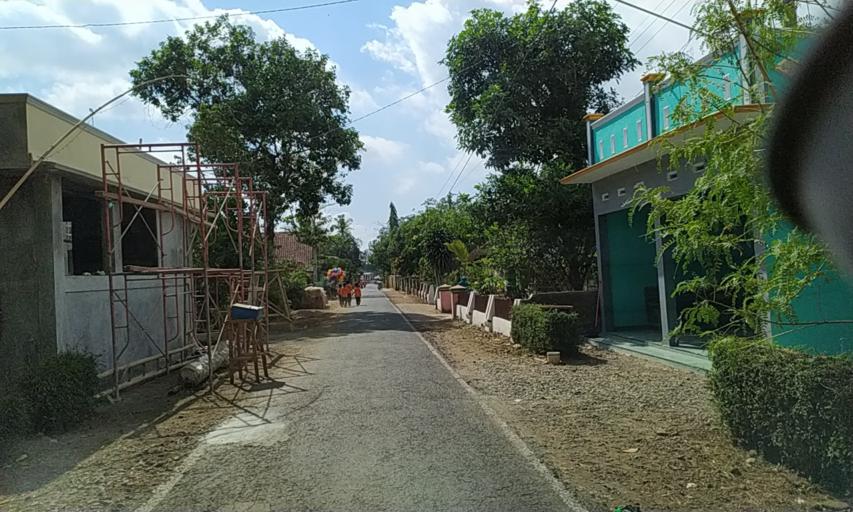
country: ID
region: Central Java
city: Kroya
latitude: -7.6275
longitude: 109.2762
